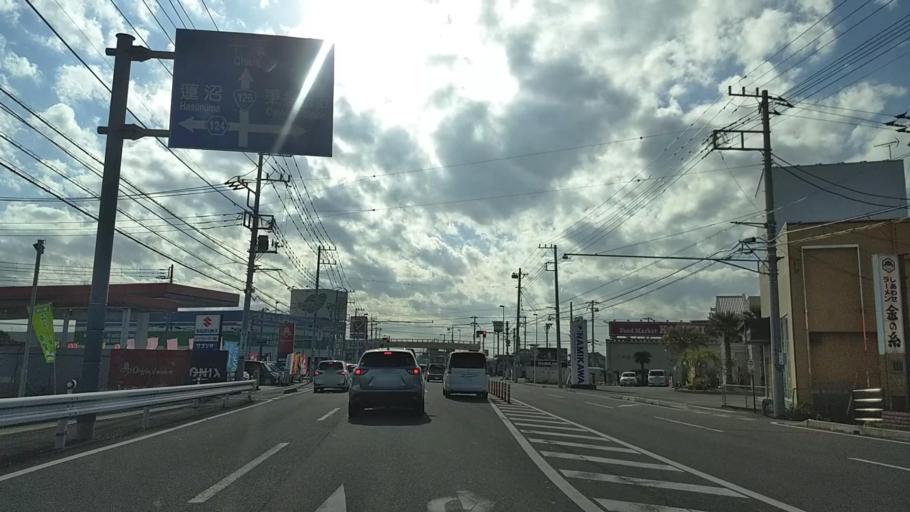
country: JP
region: Chiba
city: Togane
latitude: 35.5772
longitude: 140.3820
